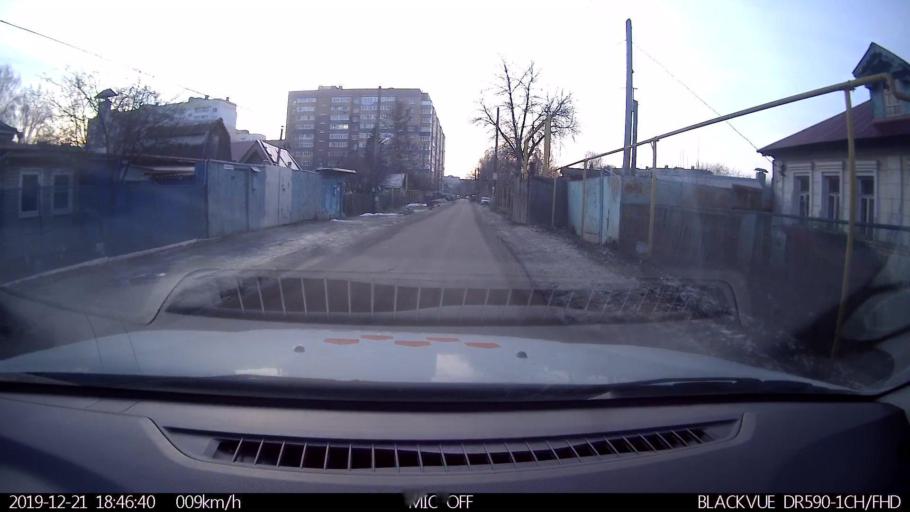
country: RU
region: Nizjnij Novgorod
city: Nizhniy Novgorod
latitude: 56.3282
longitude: 43.9251
